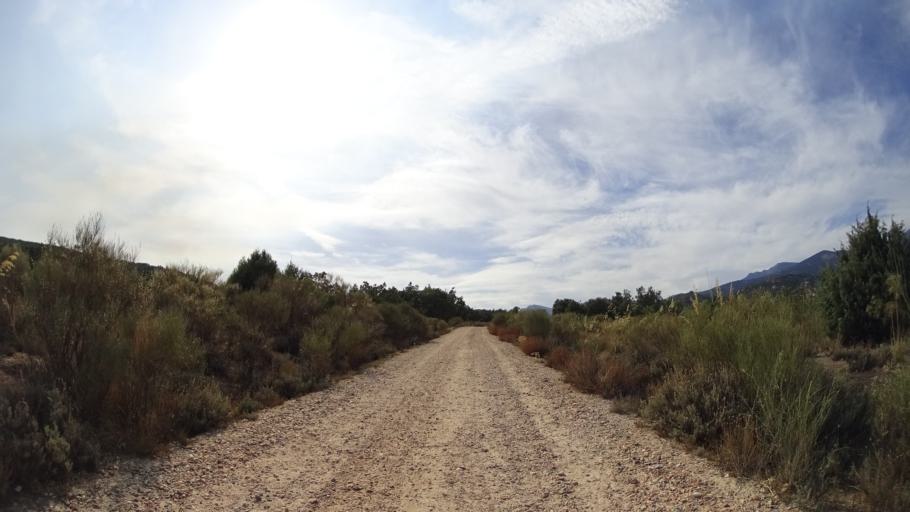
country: ES
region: Madrid
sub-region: Provincia de Madrid
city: Becerril de la Sierra
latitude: 40.6992
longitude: -3.9771
